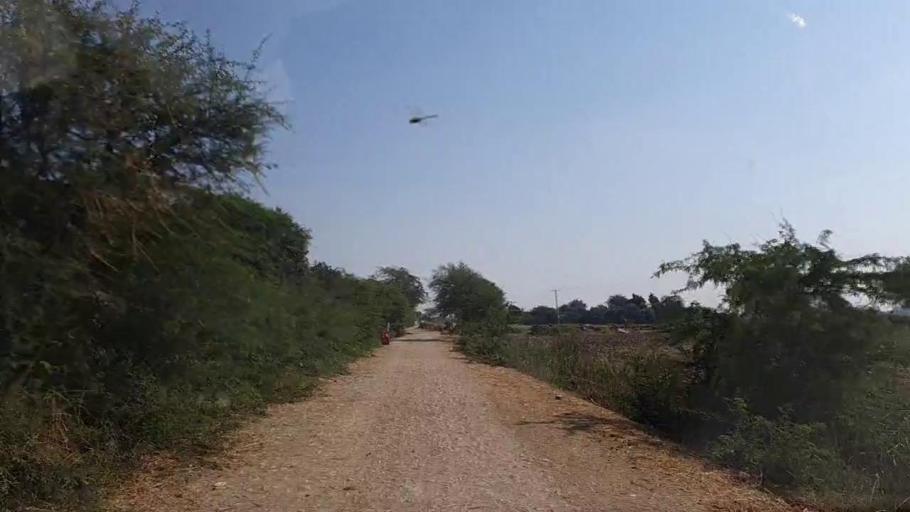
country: PK
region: Sindh
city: Thatta
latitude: 24.7652
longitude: 67.9438
